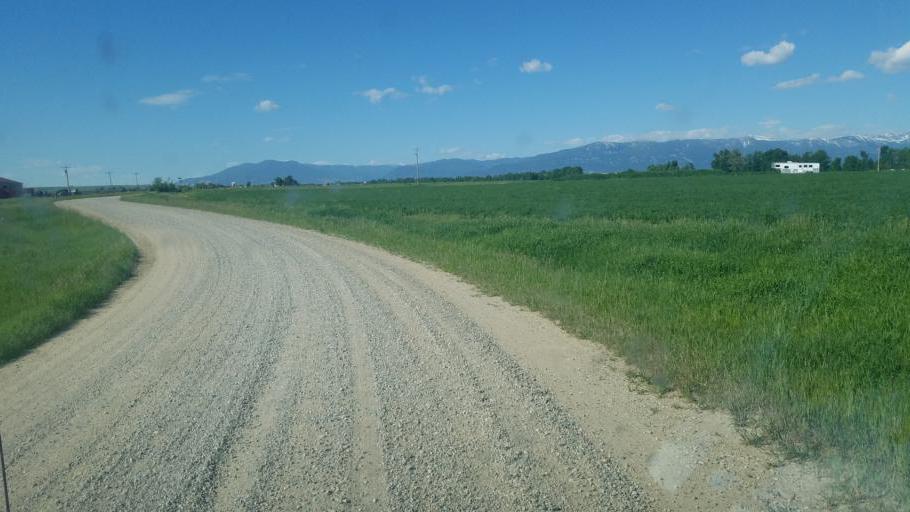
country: US
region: Montana
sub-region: Carbon County
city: Red Lodge
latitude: 45.3275
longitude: -109.1715
